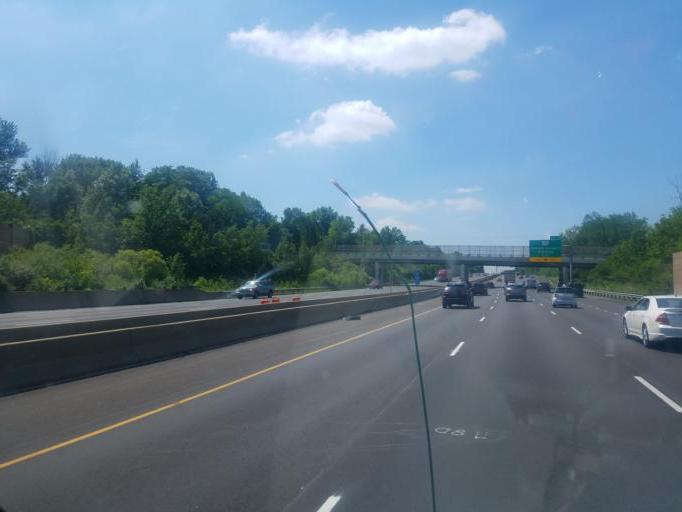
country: US
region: Ohio
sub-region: Hamilton County
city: Blue Ash
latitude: 39.2431
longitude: -84.3663
